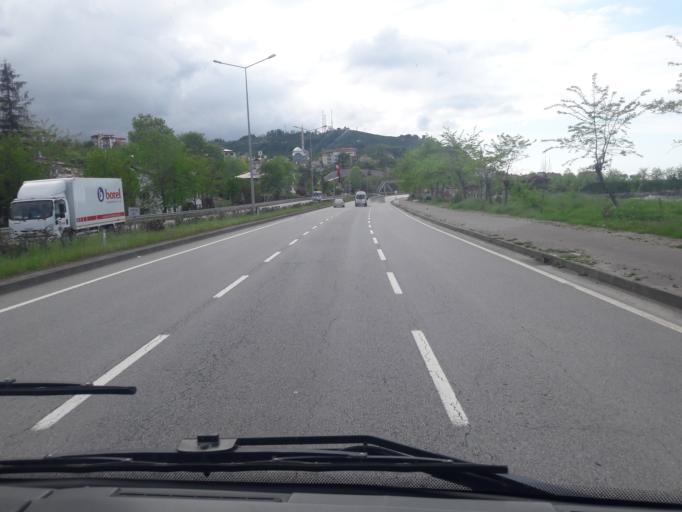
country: TR
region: Giresun
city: Piraziz
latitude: 40.9535
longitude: 38.1262
